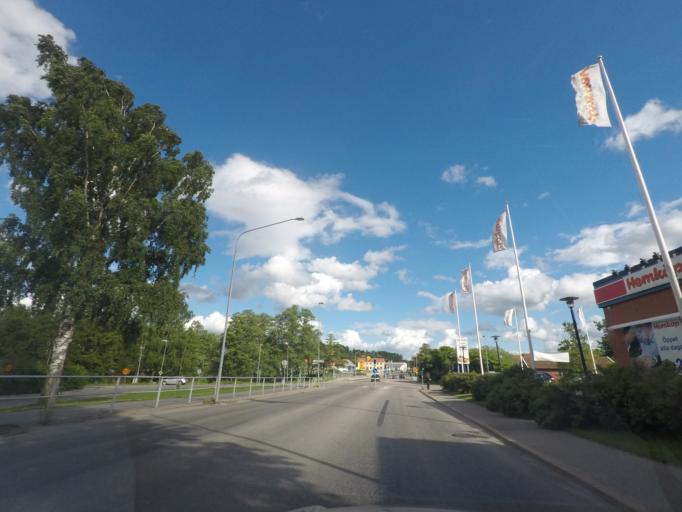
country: SE
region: OErebro
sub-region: Lindesbergs Kommun
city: Lindesberg
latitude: 59.5994
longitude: 15.2209
